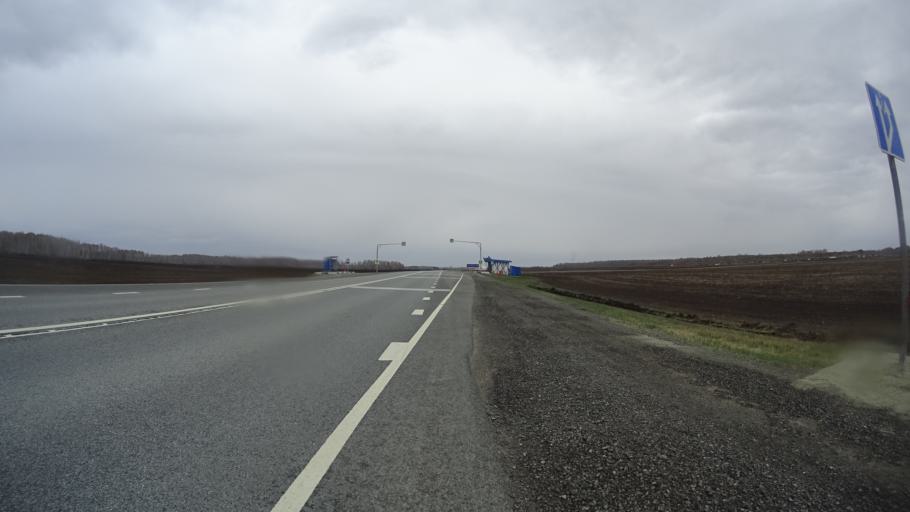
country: RU
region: Chelyabinsk
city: Krasnogorskiy
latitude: 54.5826
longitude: 61.2911
